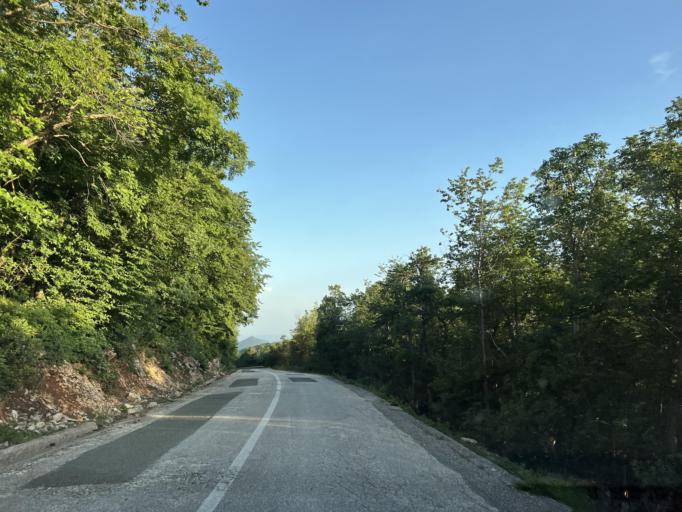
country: HR
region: Primorsko-Goranska
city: Skrljevo
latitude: 45.3875
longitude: 14.5598
